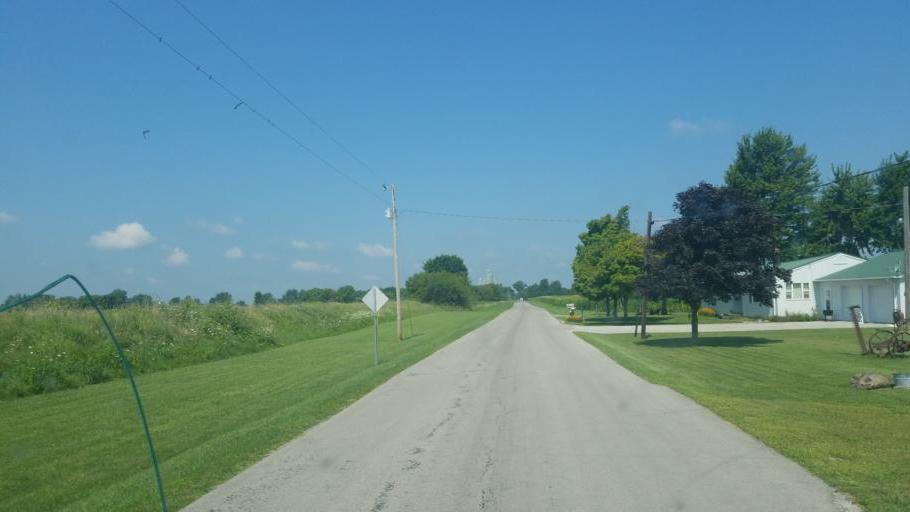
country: US
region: Ohio
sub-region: Hardin County
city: Kenton
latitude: 40.6771
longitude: -83.7308
